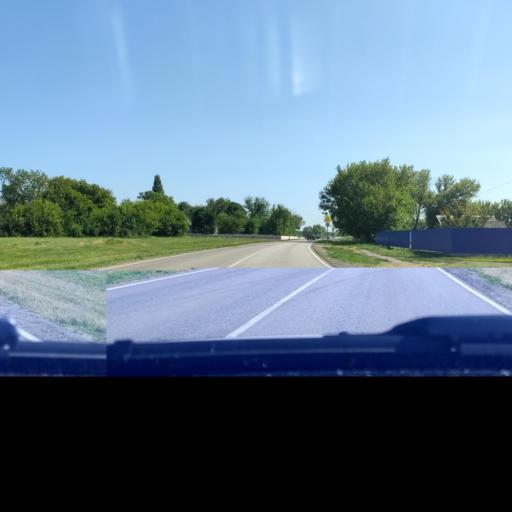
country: RU
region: Voronezj
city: Verkhnyaya Khava
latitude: 51.6807
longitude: 39.9409
